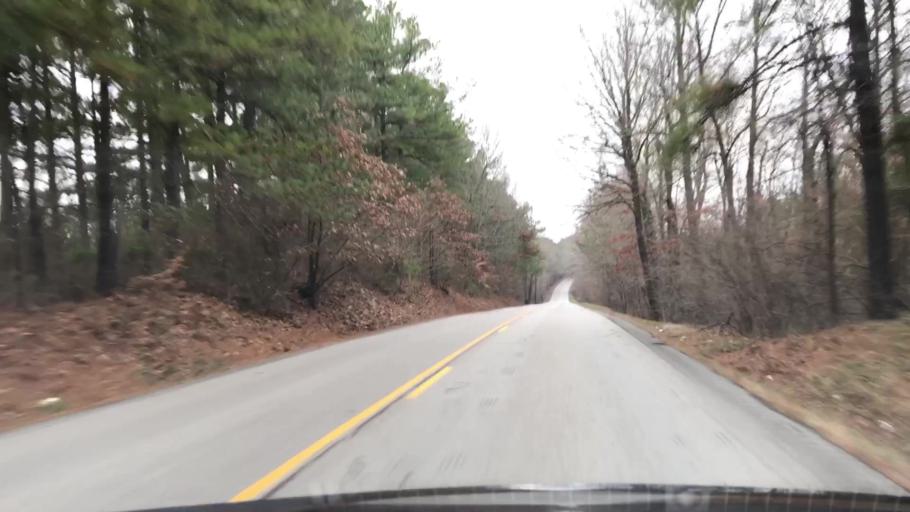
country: US
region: Kentucky
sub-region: Muhlenberg County
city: Morehead
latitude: 37.2830
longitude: -87.2096
